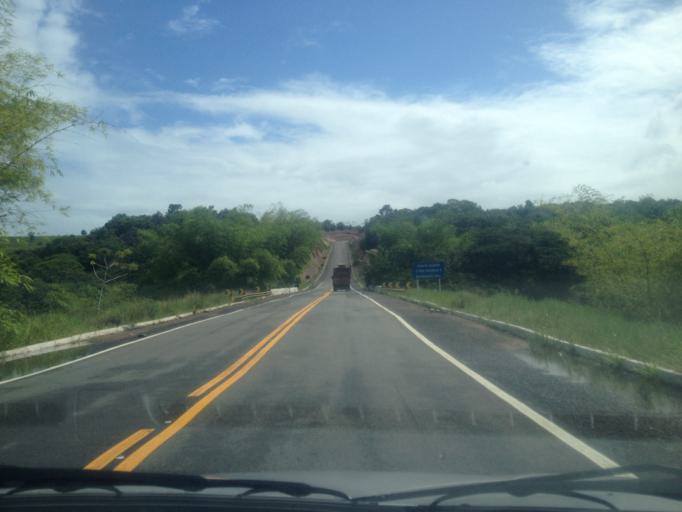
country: BR
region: Sergipe
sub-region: Indiaroba
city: Indiaroba
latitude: -11.5640
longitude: -37.5672
